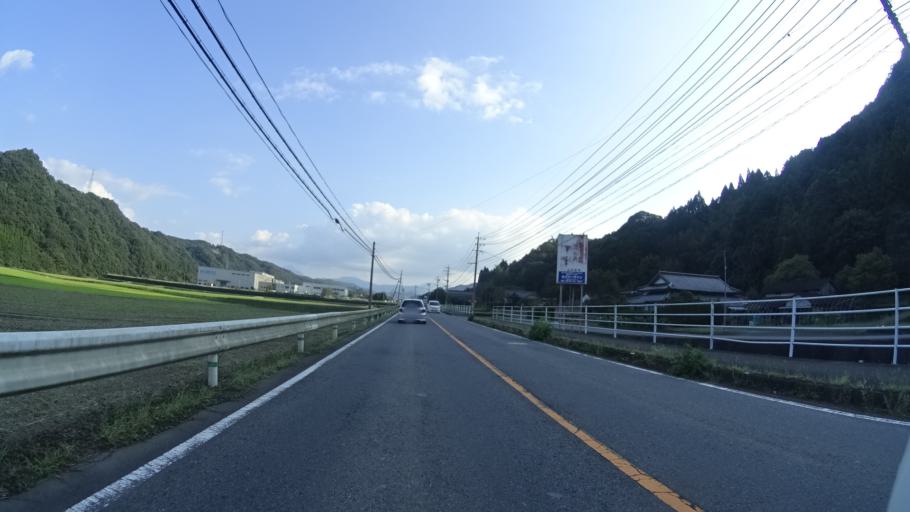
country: JP
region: Oita
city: Bungo-Takada-shi
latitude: 33.4714
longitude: 131.3279
